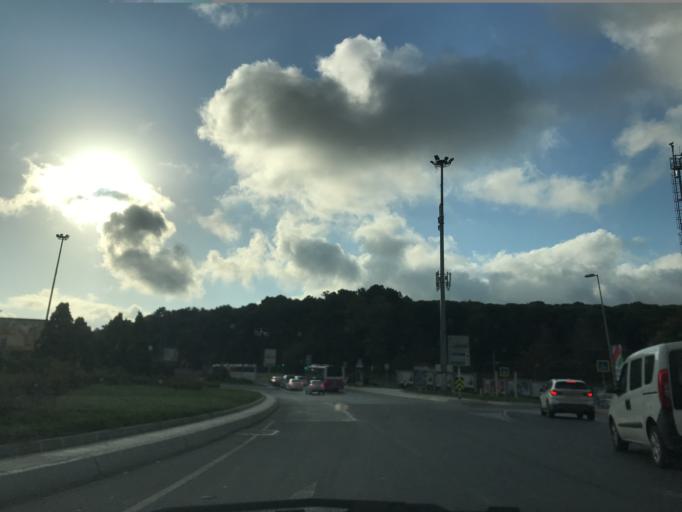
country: TR
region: Istanbul
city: Sisli
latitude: 41.1405
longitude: 29.0291
